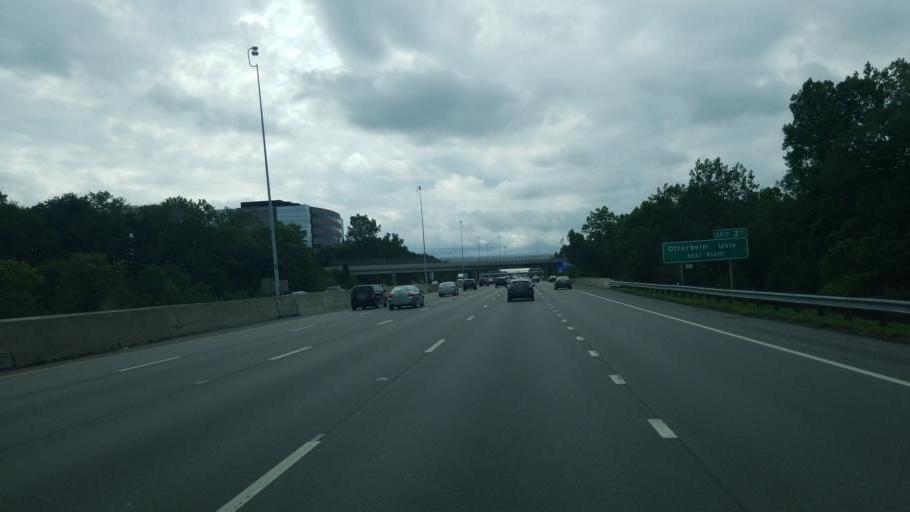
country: US
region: Ohio
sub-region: Franklin County
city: Westerville
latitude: 40.1032
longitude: -82.9369
